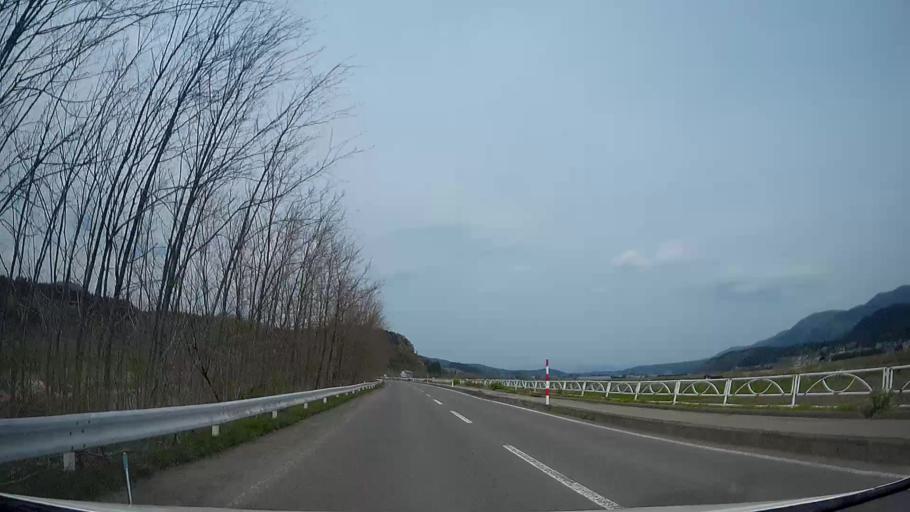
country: JP
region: Akita
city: Hanawa
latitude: 40.1068
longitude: 140.7815
